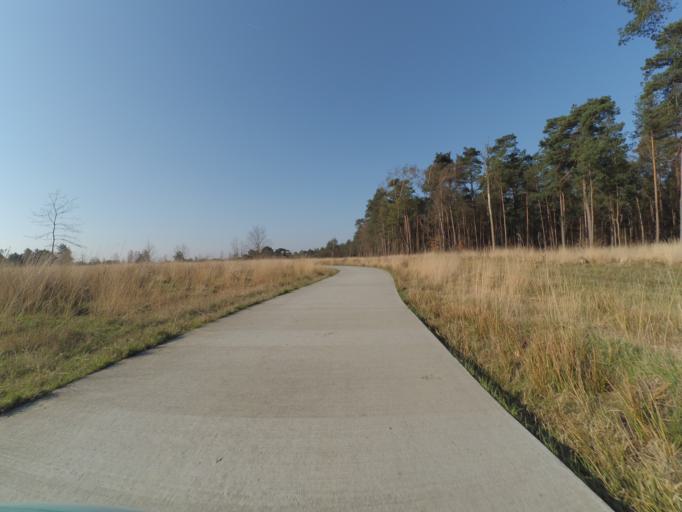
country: NL
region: Gelderland
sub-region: Gemeente Ede
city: Otterlo
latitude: 52.0952
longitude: 5.8560
